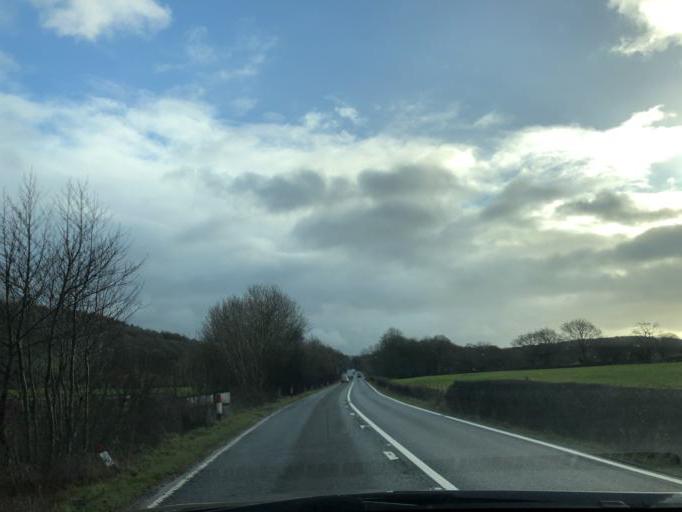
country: GB
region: England
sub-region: Cumbria
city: Grange-over-Sands
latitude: 54.2621
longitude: -2.9598
